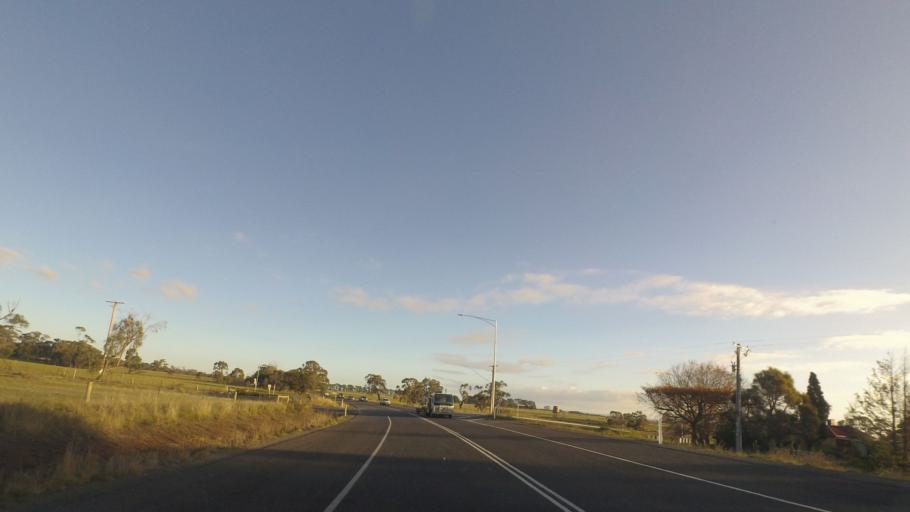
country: AU
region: Victoria
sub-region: Mount Alexander
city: Castlemaine
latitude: -37.1843
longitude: 144.4753
